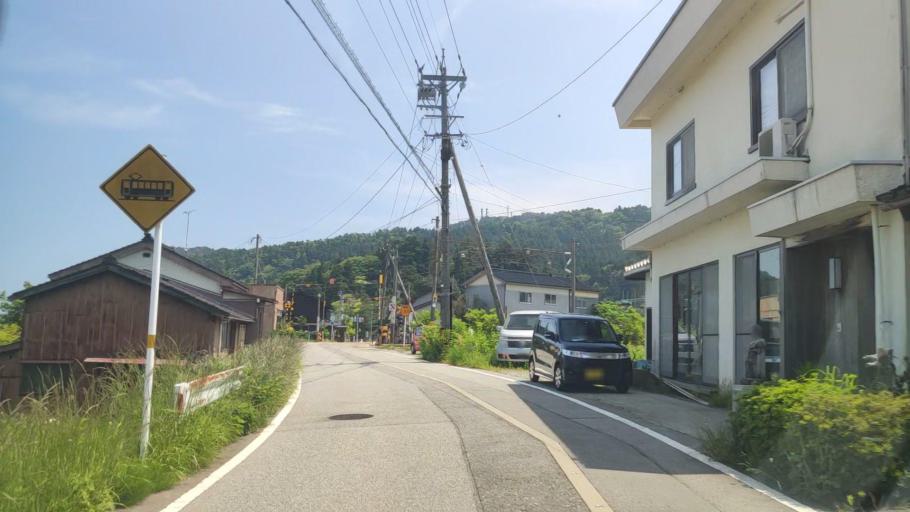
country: JP
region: Toyama
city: Nyuzen
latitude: 36.9575
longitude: 137.5686
